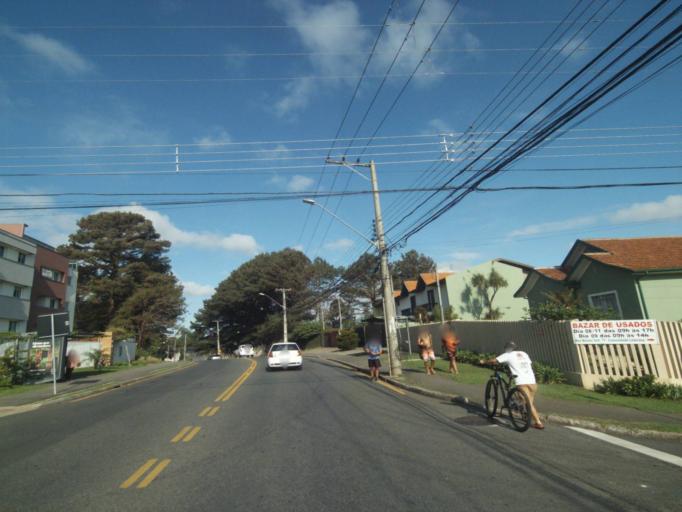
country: BR
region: Parana
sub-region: Curitiba
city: Curitiba
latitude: -25.3937
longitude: -49.2918
